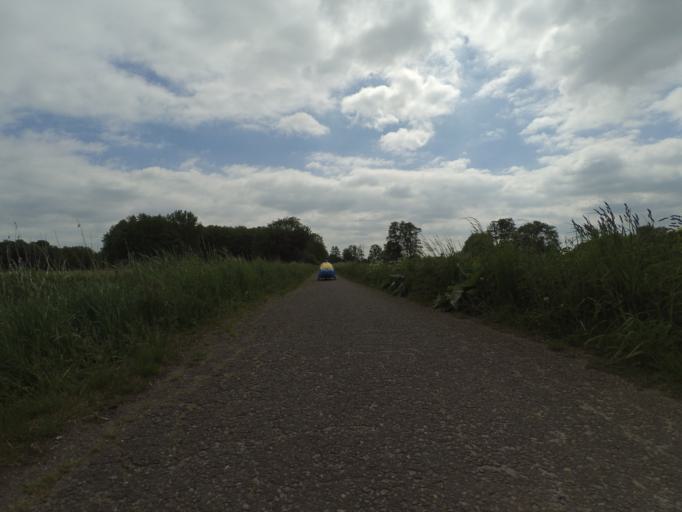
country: DE
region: Lower Saxony
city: Burgdorf
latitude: 52.4271
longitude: 10.0063
